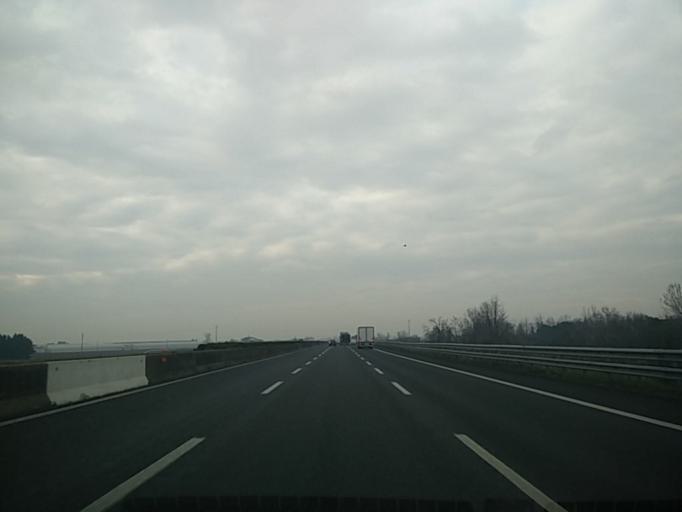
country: IT
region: Emilia-Romagna
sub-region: Provincia di Rimini
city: Santarcangelo
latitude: 44.0930
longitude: 12.4533
